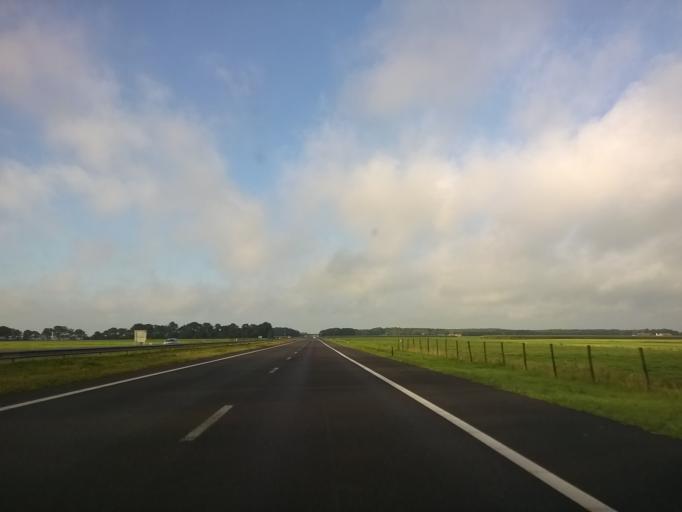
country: NL
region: Friesland
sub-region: Gemeente Achtkarspelen
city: Surhuisterveen
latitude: 53.1433
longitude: 6.2323
